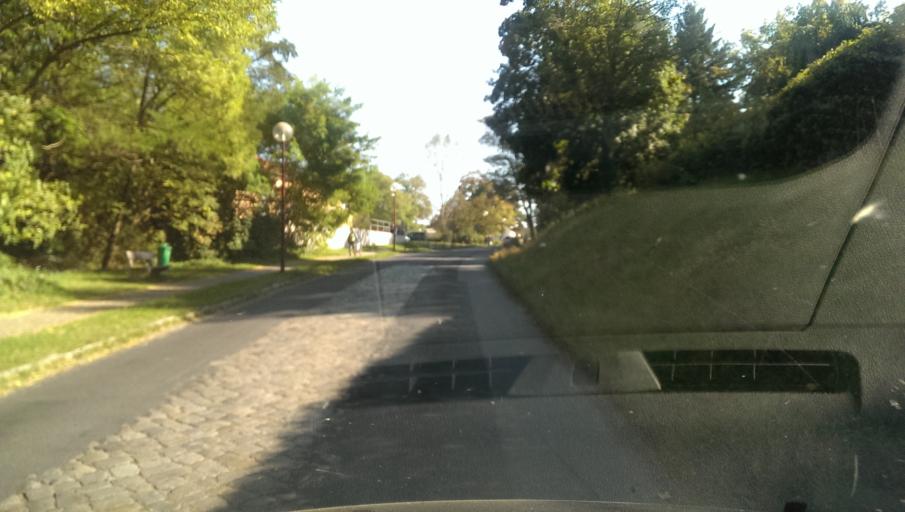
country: DE
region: Brandenburg
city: Teupitz
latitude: 52.1325
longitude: 13.6188
